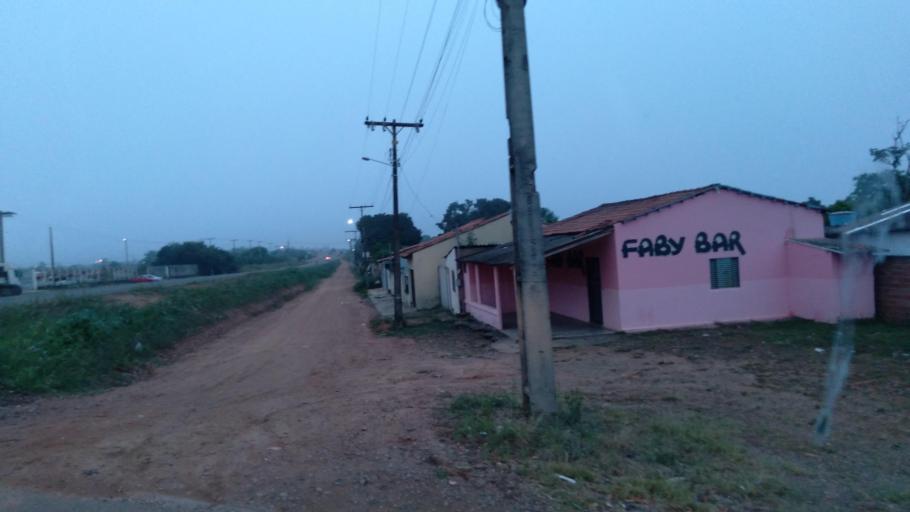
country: BR
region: Goias
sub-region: Mineiros
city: Mineiros
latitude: -17.5825
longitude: -52.5475
